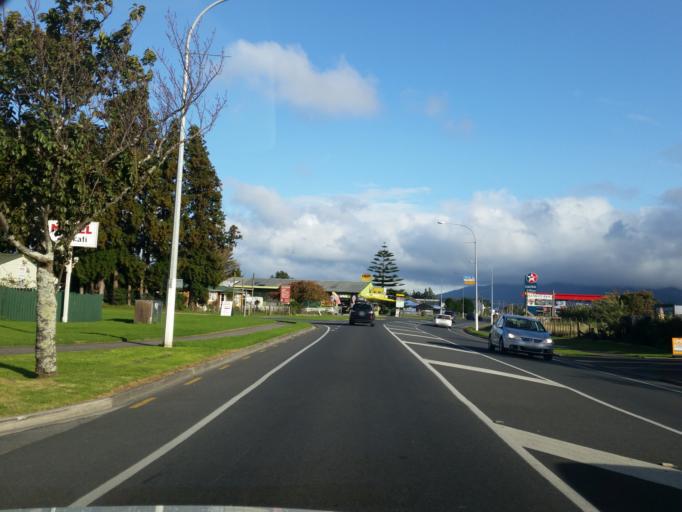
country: NZ
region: Bay of Plenty
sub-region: Western Bay of Plenty District
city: Katikati
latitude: -37.5565
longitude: 175.9169
